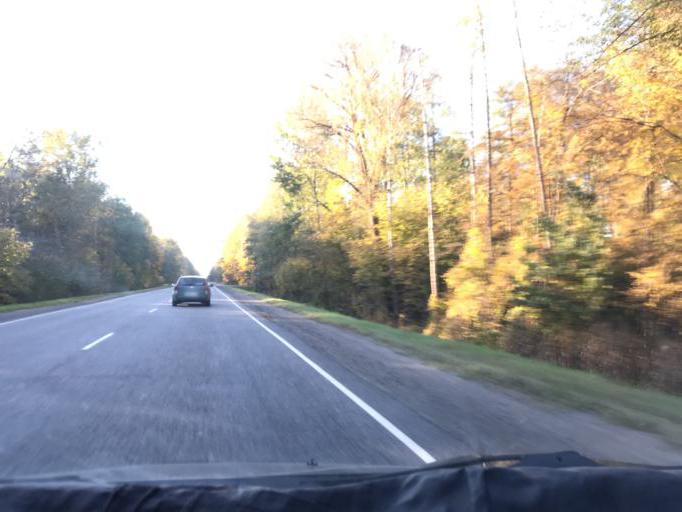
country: BY
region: Gomel
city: Pyetrykaw
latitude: 52.2633
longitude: 28.3142
